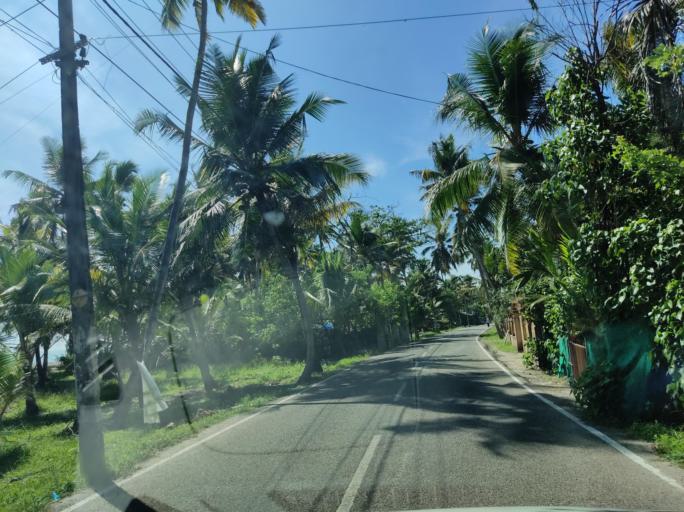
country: IN
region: Kerala
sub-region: Alappuzha
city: Kayankulam
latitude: 9.2336
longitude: 76.4193
